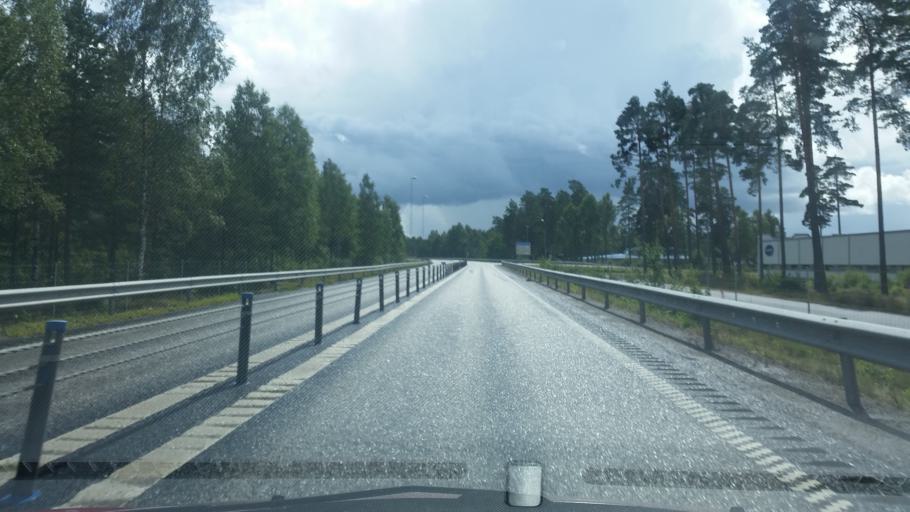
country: SE
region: Joenkoeping
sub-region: Gislaveds Kommun
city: Gislaved
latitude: 57.2761
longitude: 13.6155
